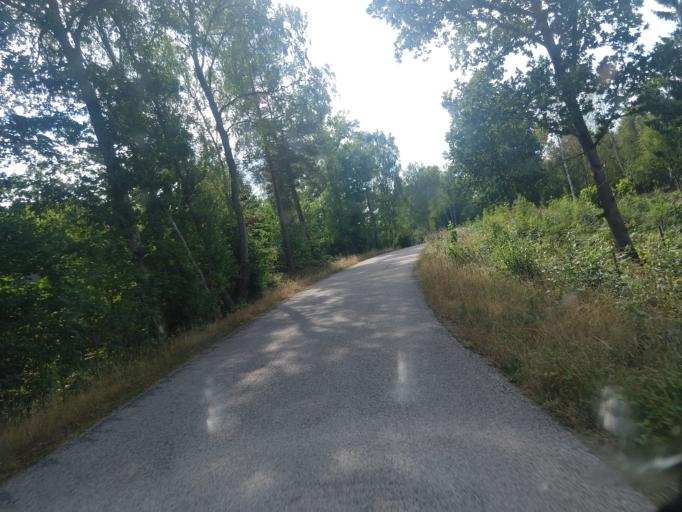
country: SE
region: Blekinge
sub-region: Karlskrona Kommun
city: Rodeby
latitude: 56.2438
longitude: 15.5488
